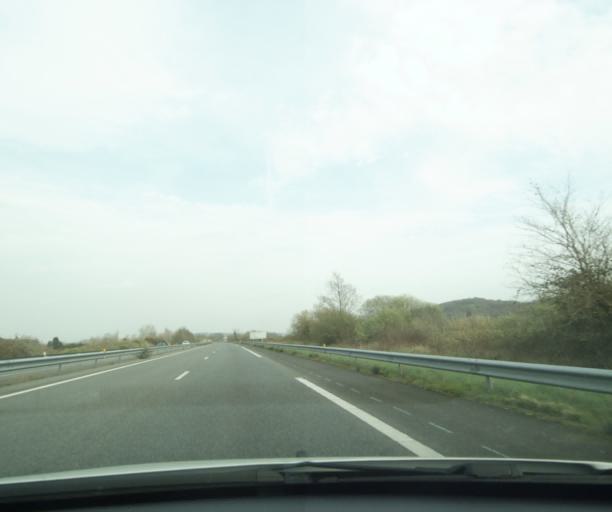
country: FR
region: Aquitaine
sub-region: Departement des Landes
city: Labatut
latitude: 43.5196
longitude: -0.9553
